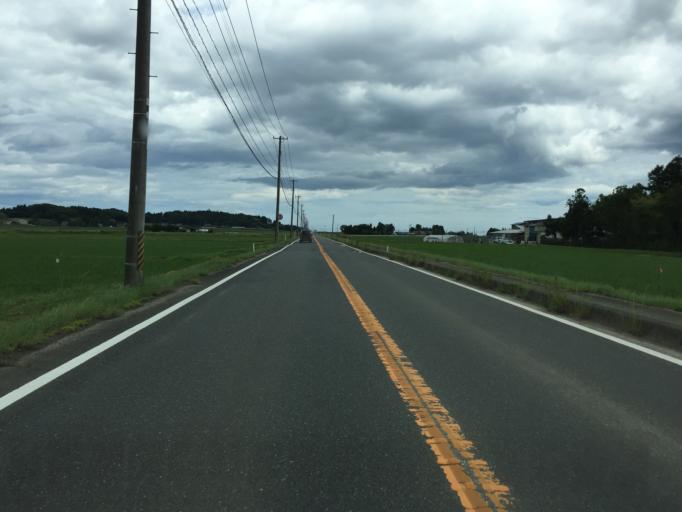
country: JP
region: Fukushima
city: Namie
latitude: 37.7067
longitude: 140.9767
